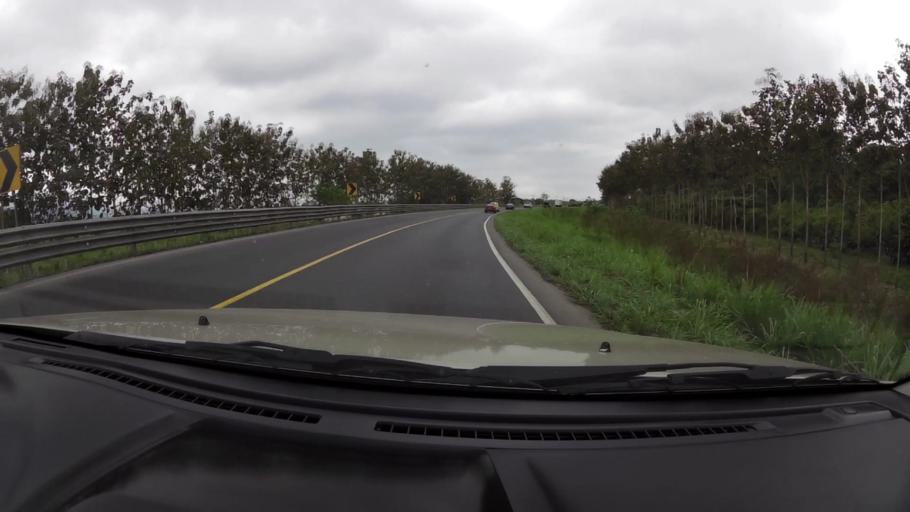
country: EC
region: Guayas
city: Naranjal
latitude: -2.7110
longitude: -79.6605
